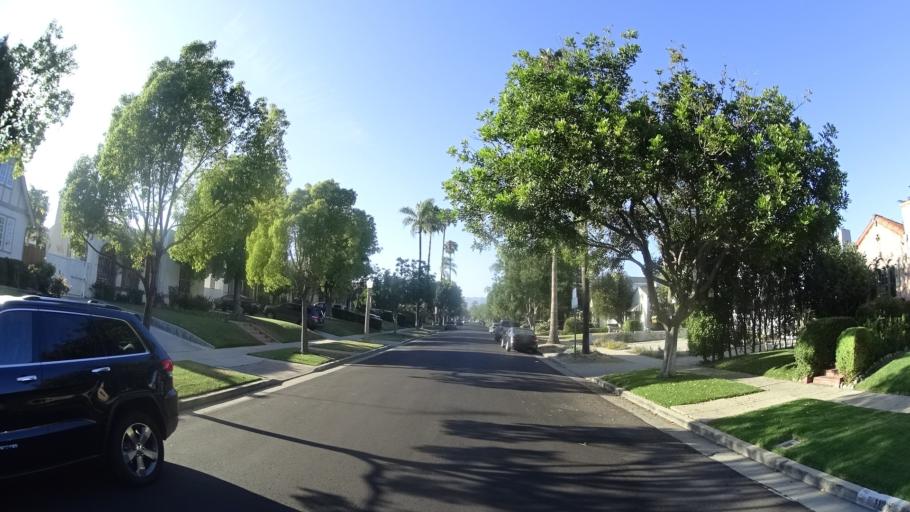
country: US
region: California
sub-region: Los Angeles County
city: Hollywood
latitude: 34.0739
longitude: -118.3215
